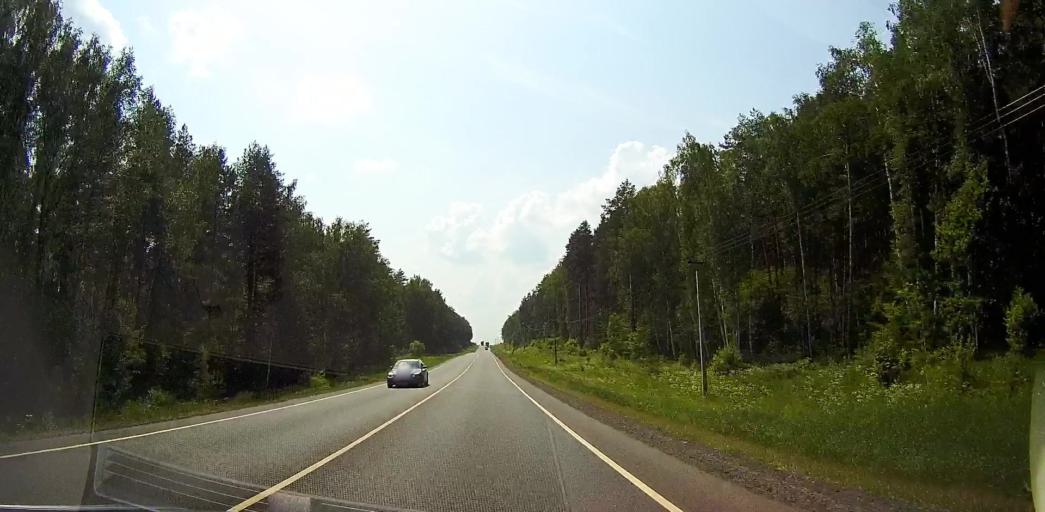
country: RU
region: Moskovskaya
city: Meshcherino
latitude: 55.1636
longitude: 38.3183
